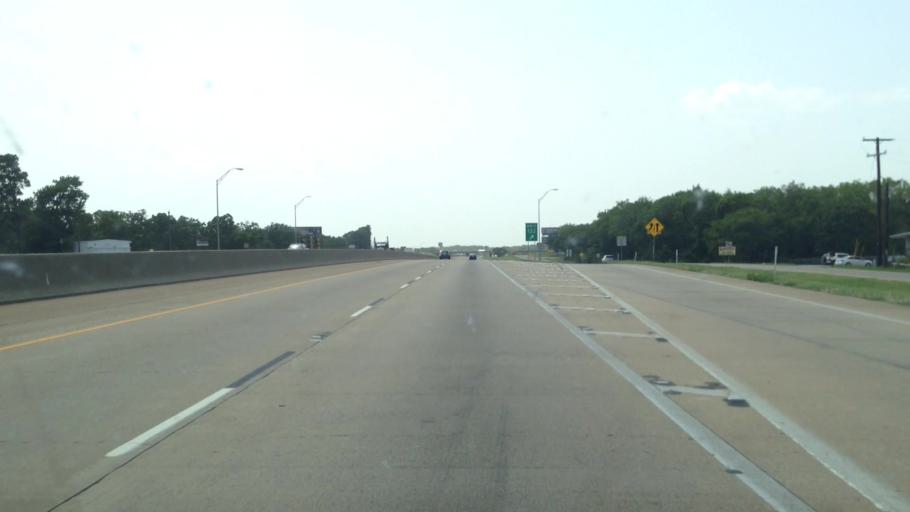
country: US
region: Texas
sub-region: Hopkins County
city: Sulphur Springs
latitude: 33.1183
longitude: -95.6251
